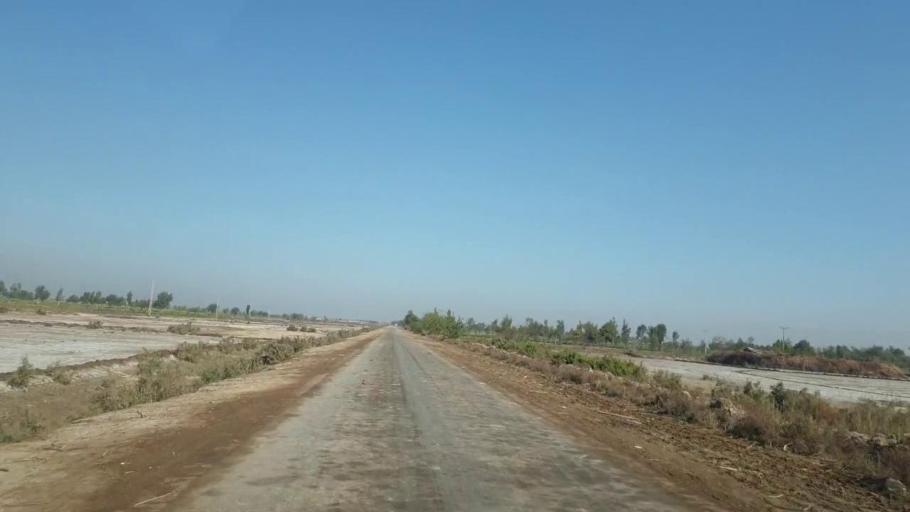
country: PK
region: Sindh
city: Mirpur Khas
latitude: 25.5842
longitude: 69.0456
